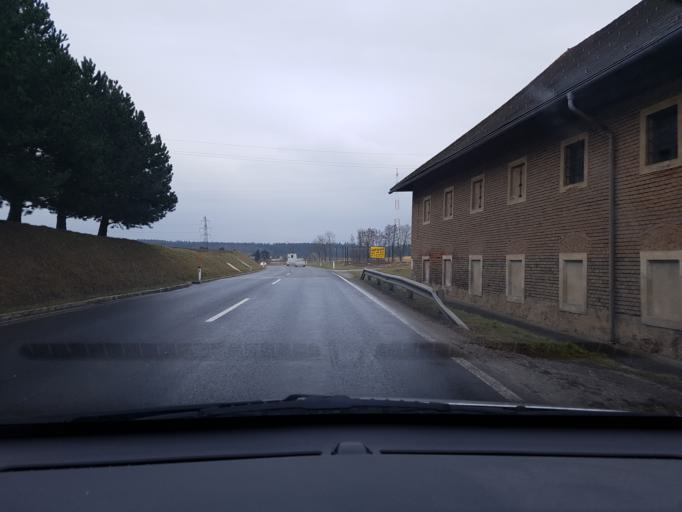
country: AT
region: Upper Austria
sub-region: Steyr Stadt
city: Steyr
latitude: 48.0754
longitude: 14.3817
